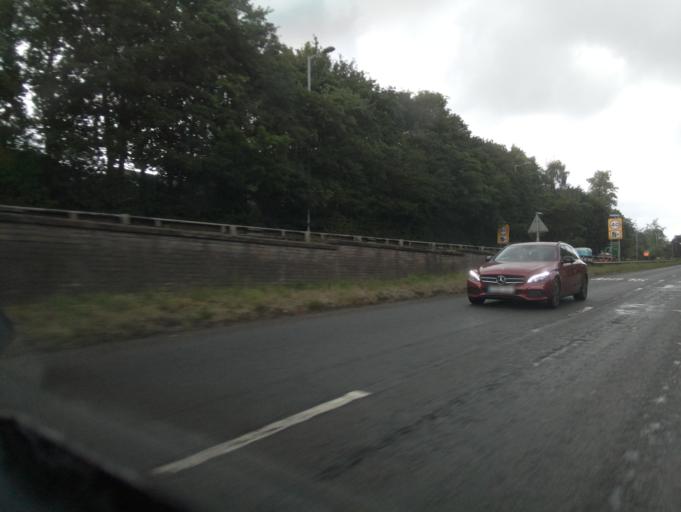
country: GB
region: England
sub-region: Dudley
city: Kingswinford
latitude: 52.5515
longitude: -2.1715
